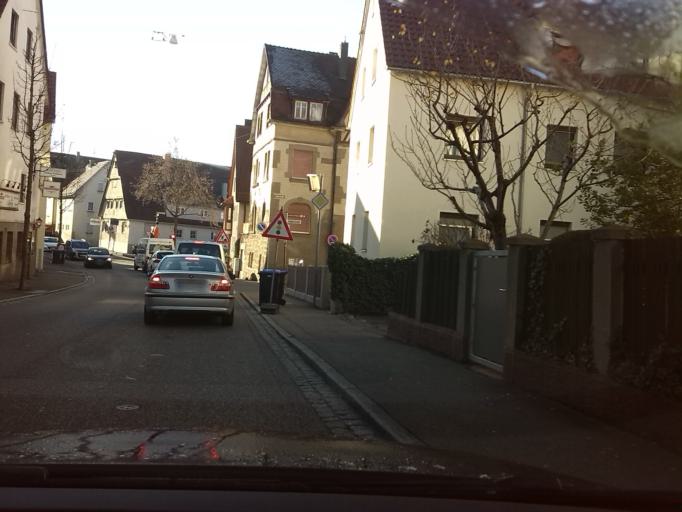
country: DE
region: Baden-Wuerttemberg
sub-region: Regierungsbezirk Stuttgart
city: Fellbach
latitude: 48.8047
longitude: 9.2777
